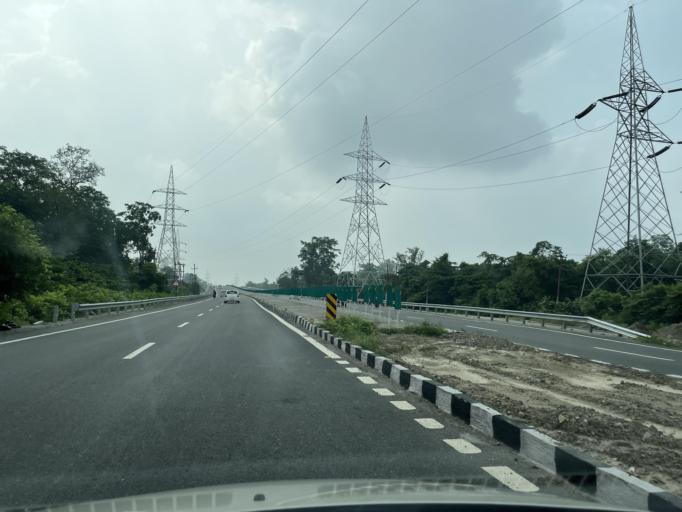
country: IN
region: Uttarakhand
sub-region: Dehradun
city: Raiwala
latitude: 30.1050
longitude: 78.1746
